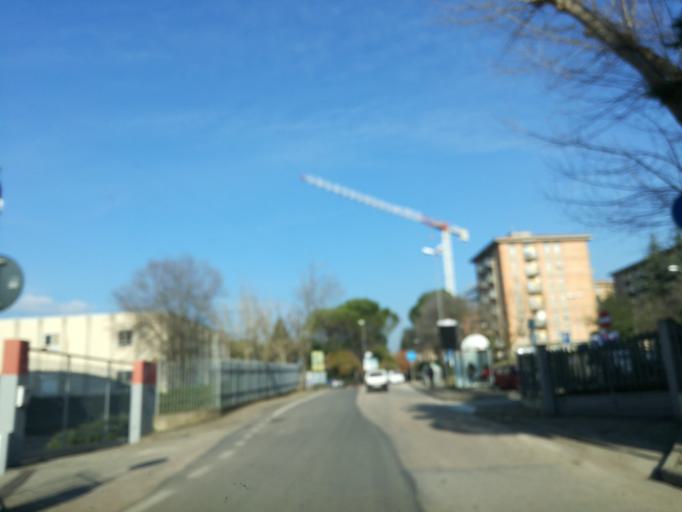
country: IT
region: Umbria
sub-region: Provincia di Perugia
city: Perugia
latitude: 43.1079
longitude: 12.3669
